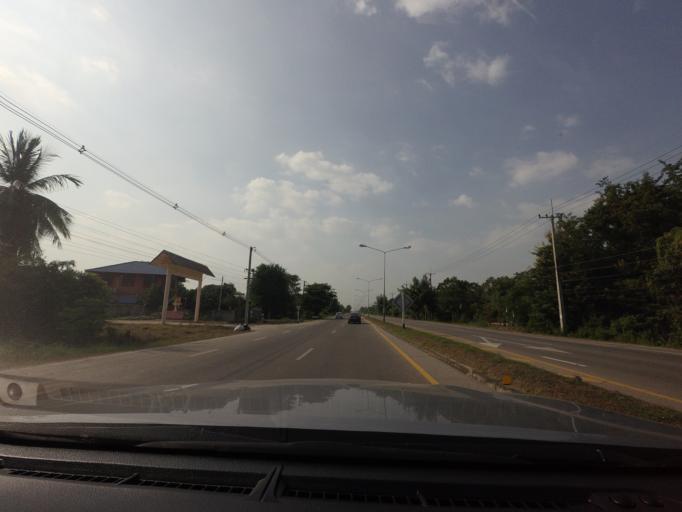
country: TH
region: Sukhothai
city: Kong Krailat
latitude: 17.0103
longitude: 99.9223
